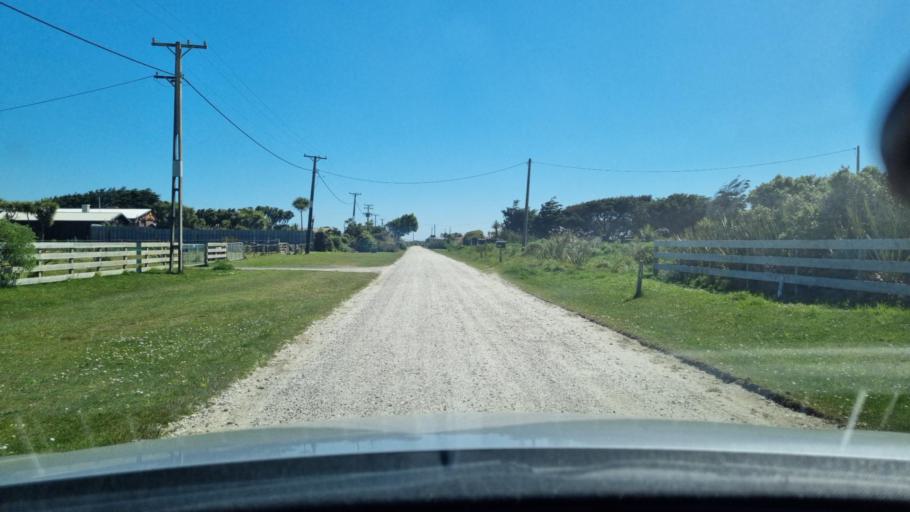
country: NZ
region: Southland
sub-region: Invercargill City
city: Invercargill
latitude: -46.4316
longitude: 168.2338
